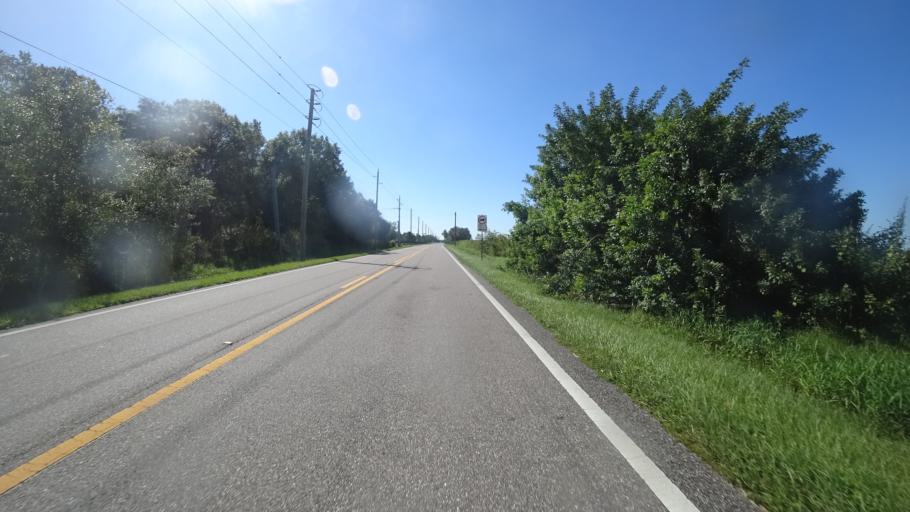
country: US
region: Florida
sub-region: Sarasota County
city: Lake Sarasota
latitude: 27.3511
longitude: -82.2687
